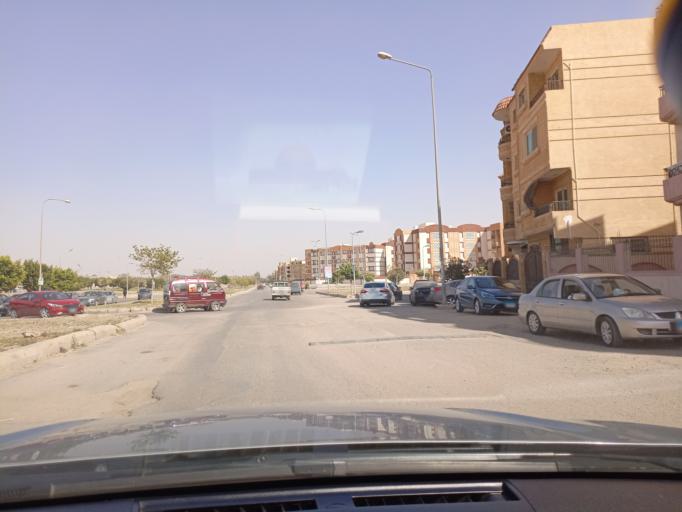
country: EG
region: Muhafazat al Qalyubiyah
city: Al Khankah
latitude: 30.2275
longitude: 31.4468
